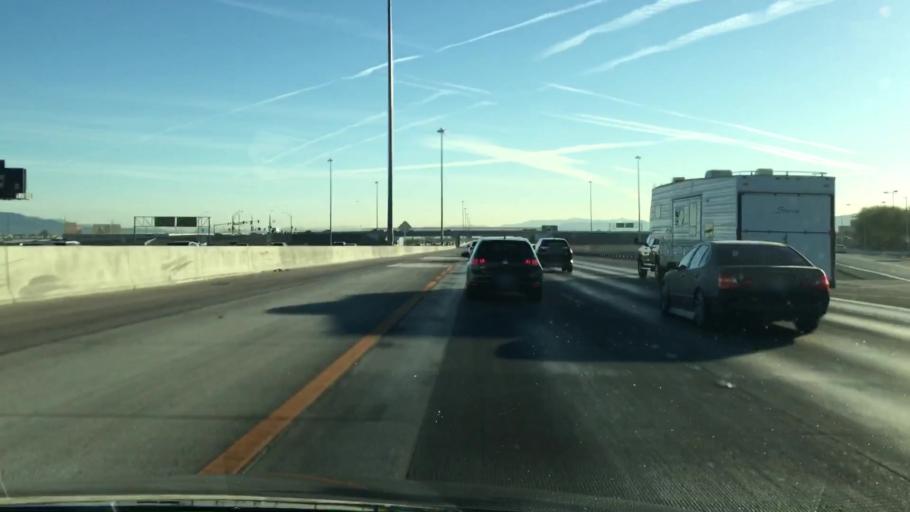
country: US
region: Nevada
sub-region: Clark County
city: Enterprise
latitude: 36.0664
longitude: -115.2474
